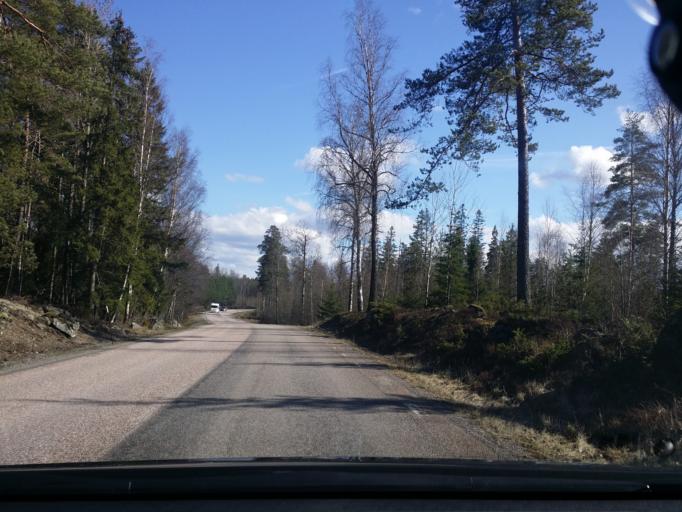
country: SE
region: Vaestmanland
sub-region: Sala Kommun
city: Sala
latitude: 59.9735
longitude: 16.4989
